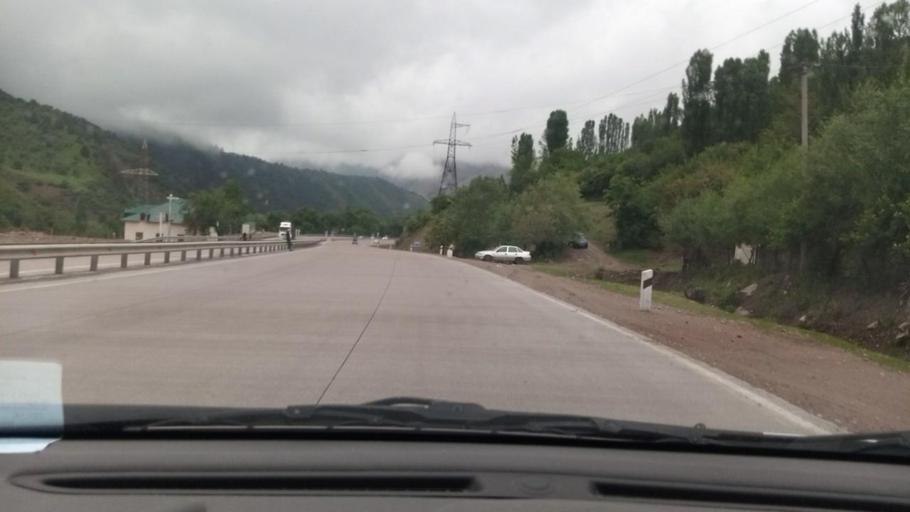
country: UZ
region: Toshkent
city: Angren
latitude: 41.1325
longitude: 70.4650
